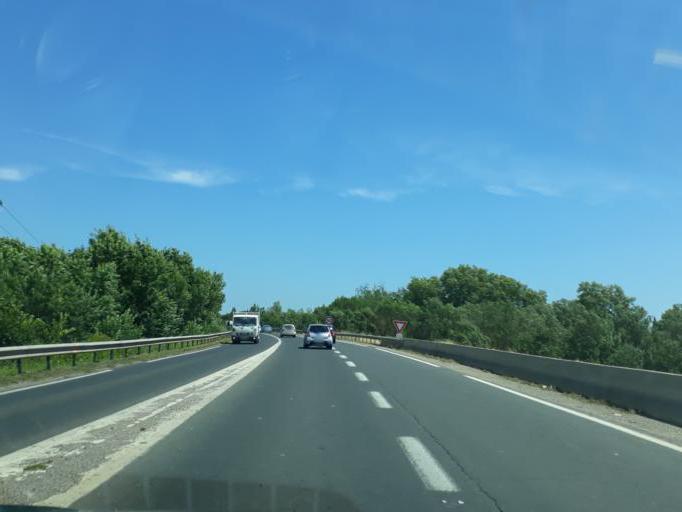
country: FR
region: Languedoc-Roussillon
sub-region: Departement de l'Herault
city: Vias
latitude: 43.3080
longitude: 3.4359
